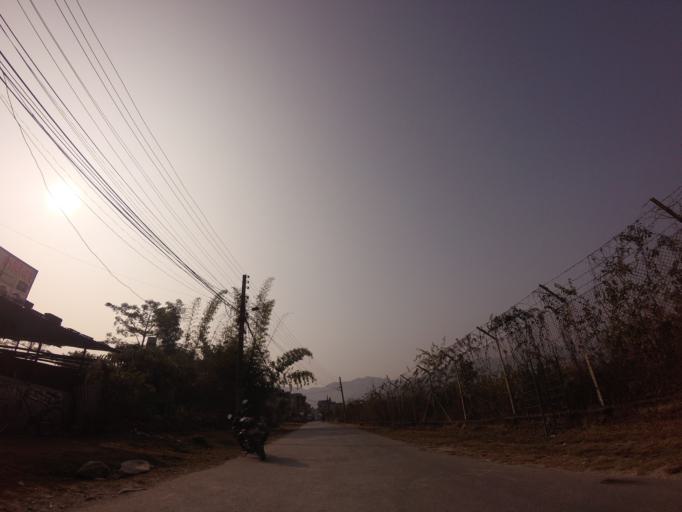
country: NP
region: Western Region
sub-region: Gandaki Zone
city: Pokhara
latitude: 28.1955
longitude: 83.9790
